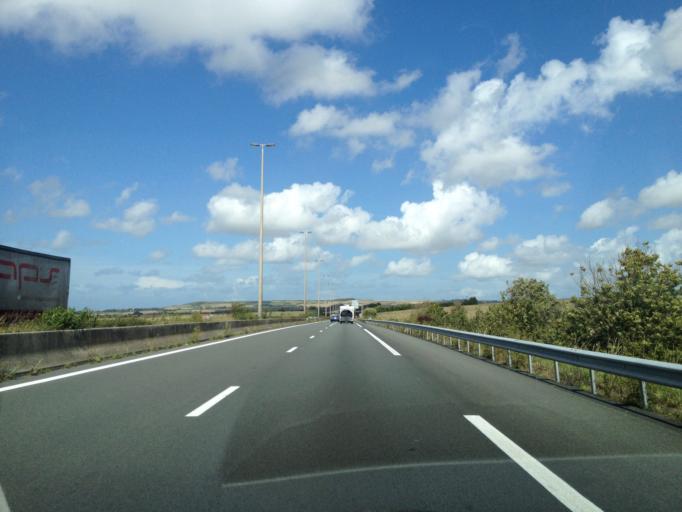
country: FR
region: Nord-Pas-de-Calais
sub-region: Departement du Pas-de-Calais
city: Marquise
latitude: 50.8216
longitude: 1.6979
